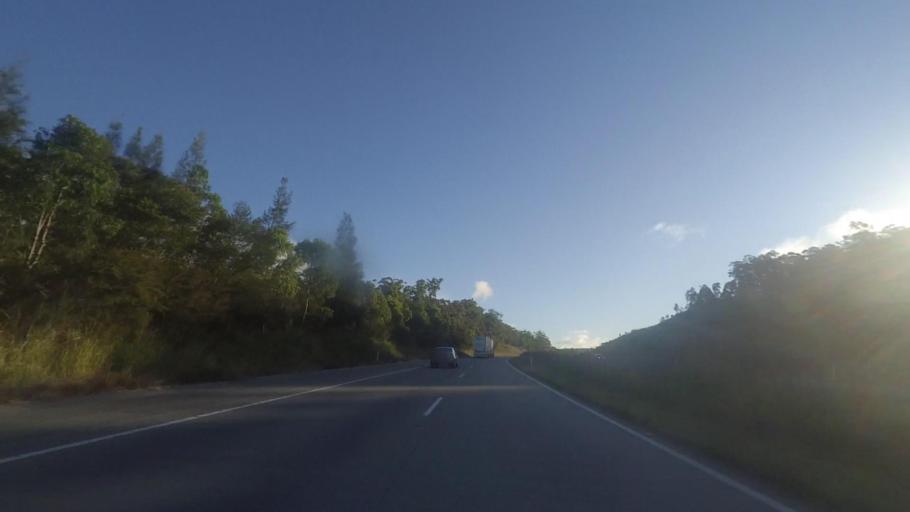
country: AU
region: New South Wales
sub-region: Great Lakes
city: Bulahdelah
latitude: -32.5140
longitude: 152.2100
